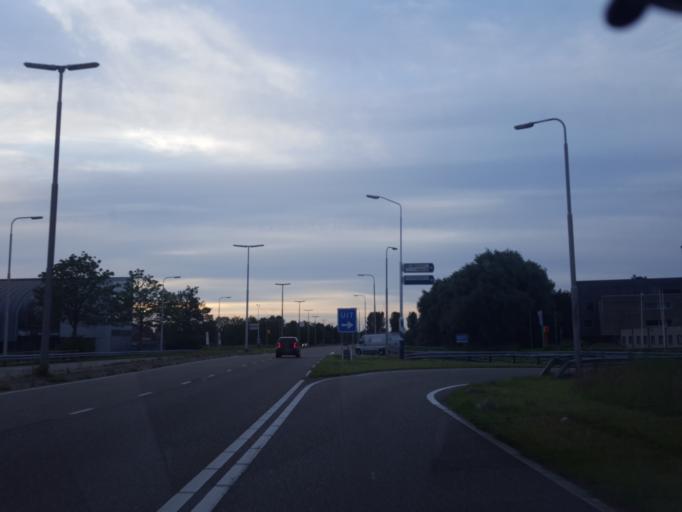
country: NL
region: Friesland
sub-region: Gemeente Leeuwarden
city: Camminghaburen
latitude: 53.2107
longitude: 5.8314
